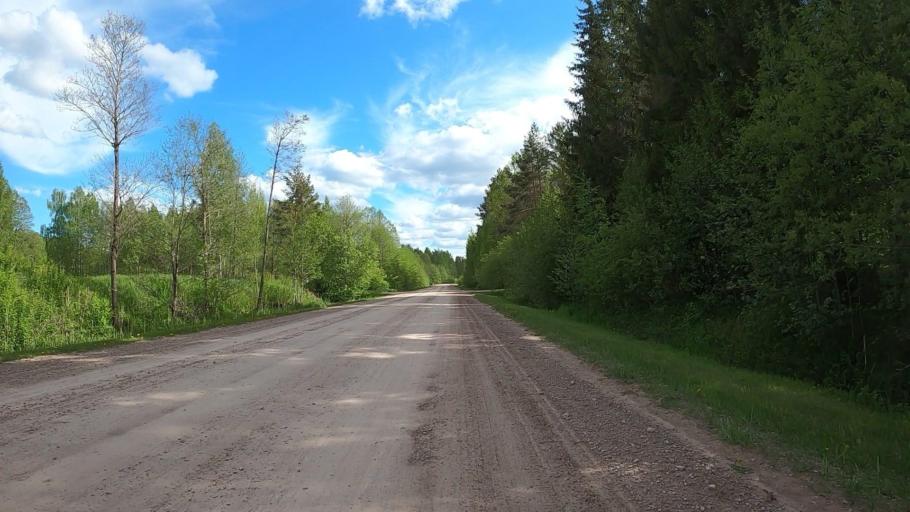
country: LV
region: Jurmala
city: Jurmala
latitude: 56.8632
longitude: 23.7877
